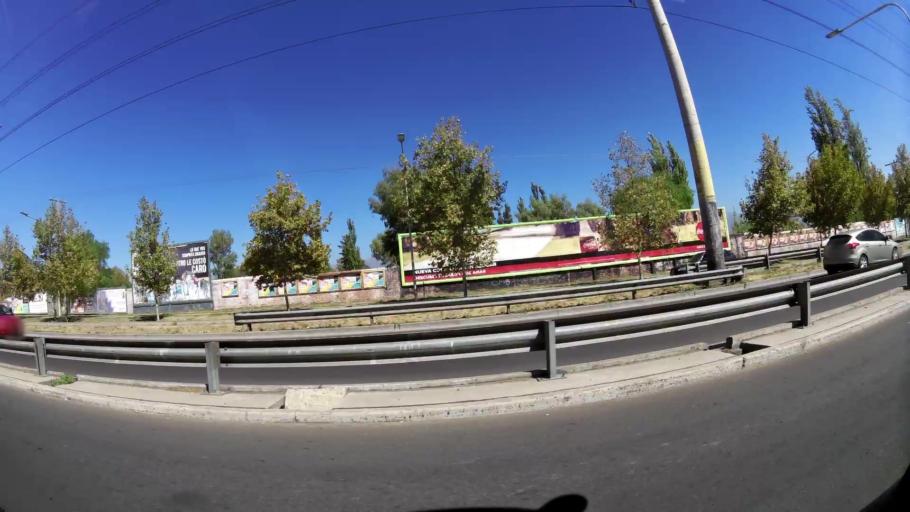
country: AR
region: Mendoza
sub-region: Departamento de Godoy Cruz
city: Godoy Cruz
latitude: -32.9138
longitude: -68.8640
